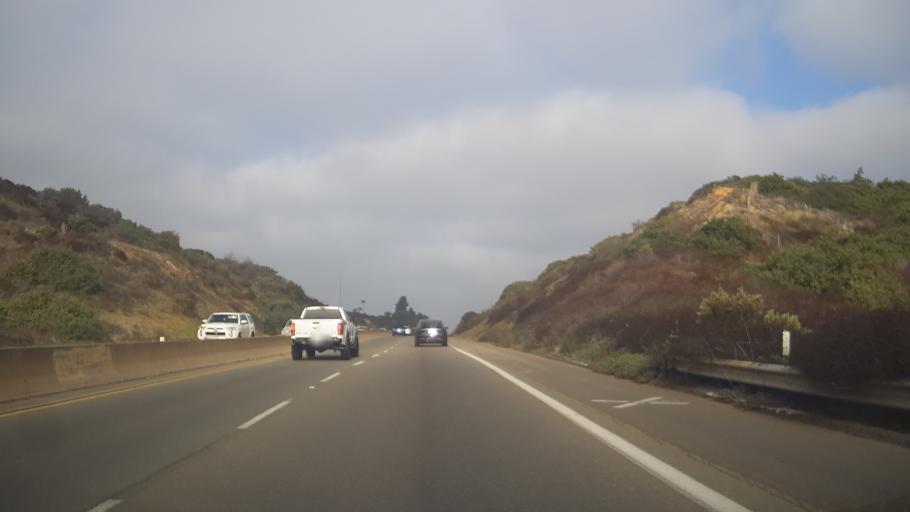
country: US
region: California
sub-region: San Diego County
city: La Jolla
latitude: 32.8411
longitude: -117.2381
